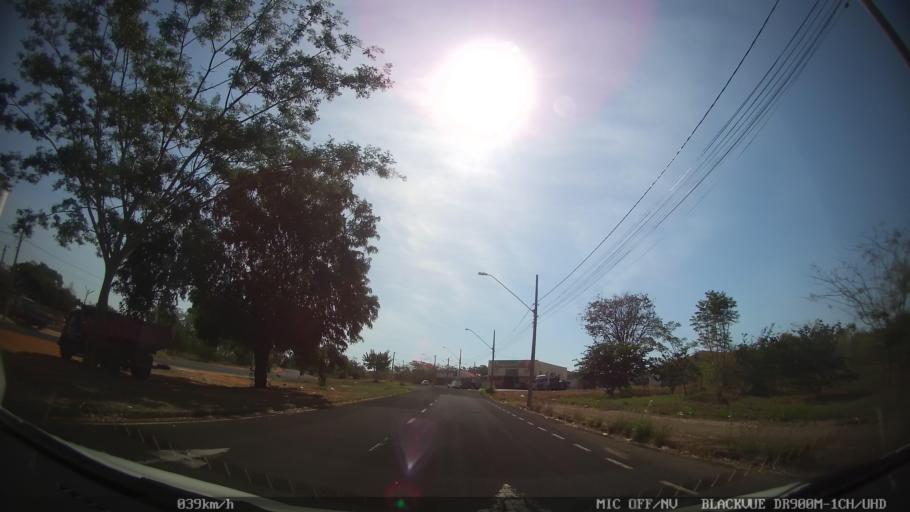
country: BR
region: Sao Paulo
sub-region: Sao Jose Do Rio Preto
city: Sao Jose do Rio Preto
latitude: -20.7856
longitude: -49.4244
